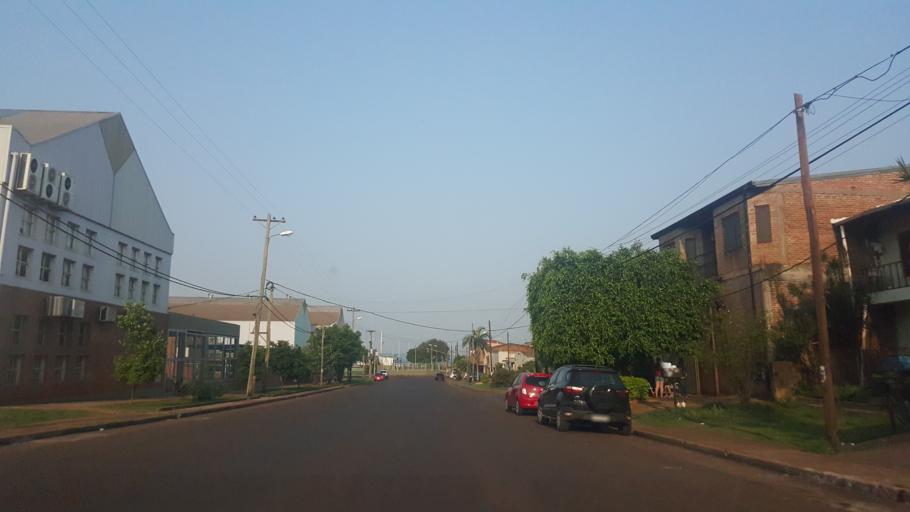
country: AR
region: Misiones
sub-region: Departamento de Capital
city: Posadas
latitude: -27.3949
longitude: -55.8960
